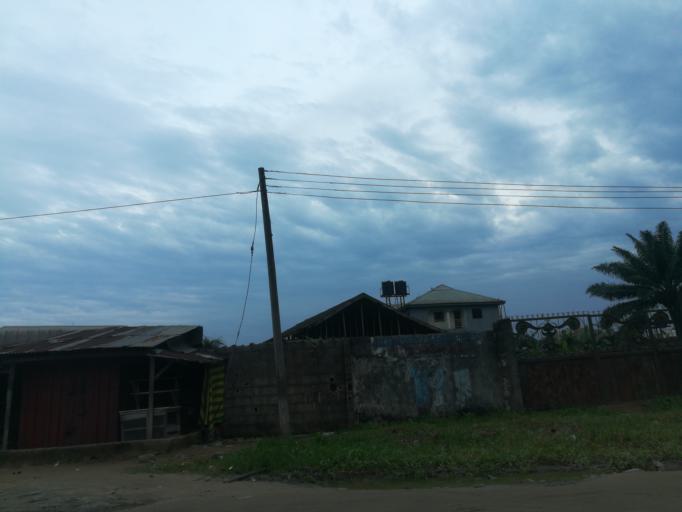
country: NG
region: Rivers
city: Port Harcourt
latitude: 4.7987
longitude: 6.9533
